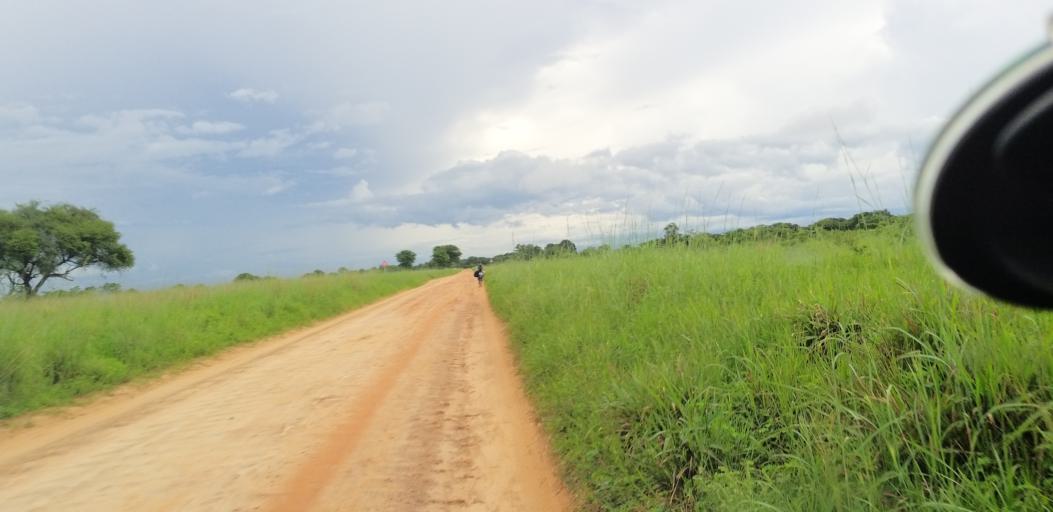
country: ZM
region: Lusaka
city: Chongwe
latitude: -15.1584
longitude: 28.4930
